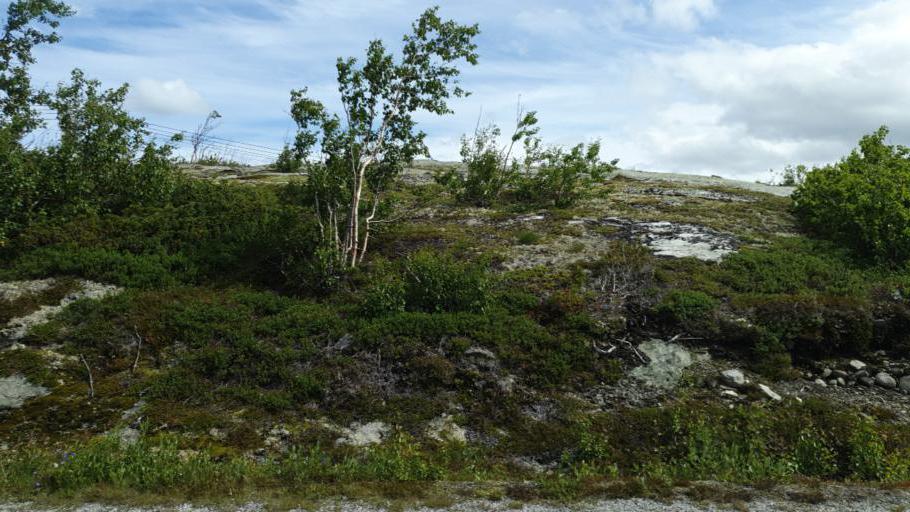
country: NO
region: Oppland
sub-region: Oystre Slidre
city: Heggenes
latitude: 61.4879
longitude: 8.8286
